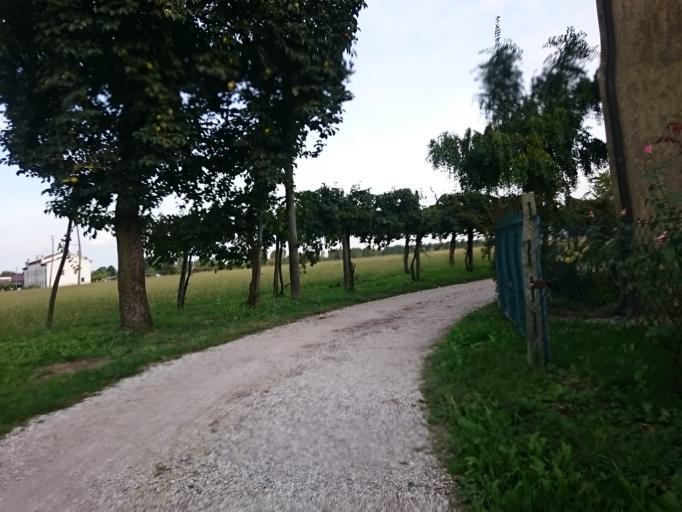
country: IT
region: Veneto
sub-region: Provincia di Vicenza
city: Grumolo delle Abbadesse
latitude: 45.5492
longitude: 11.6814
